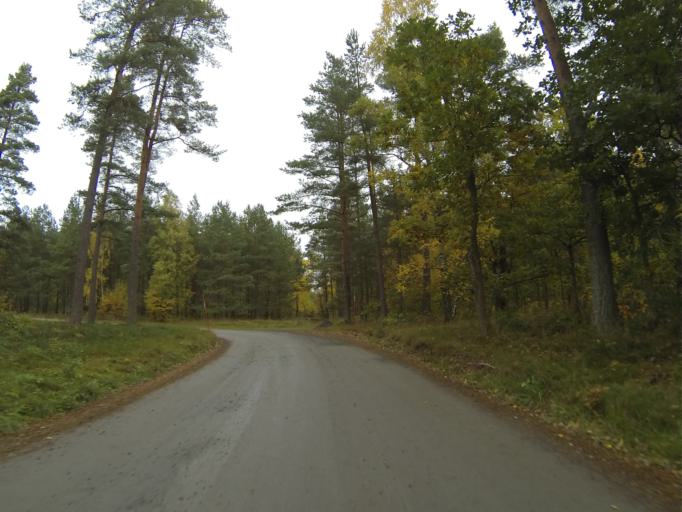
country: SE
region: Skane
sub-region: Sjobo Kommun
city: Sjoebo
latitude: 55.6347
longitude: 13.6436
